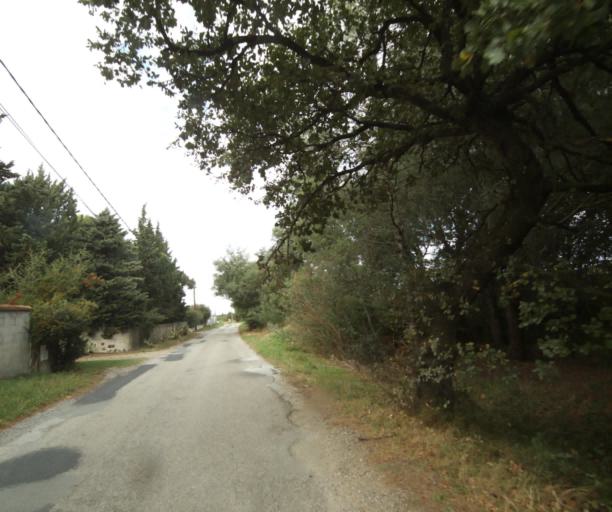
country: FR
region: Languedoc-Roussillon
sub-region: Departement des Pyrenees-Orientales
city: Sant Andreu de Sureda
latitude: 42.5468
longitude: 2.9907
